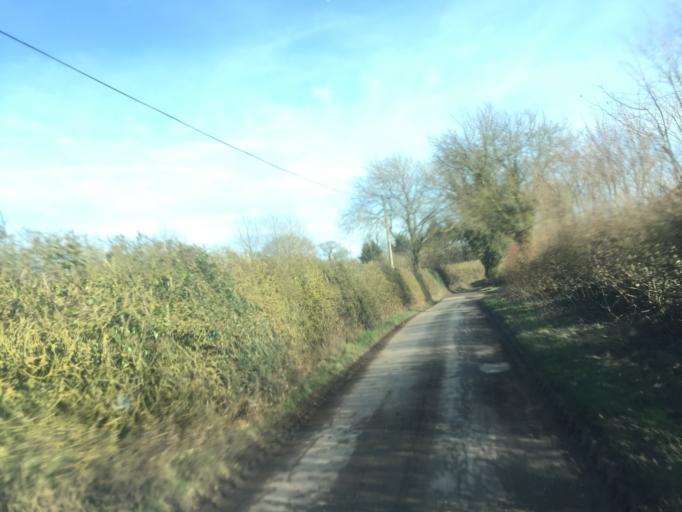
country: GB
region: England
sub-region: Shropshire
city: Bridgnorth
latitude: 52.5297
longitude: -2.4941
